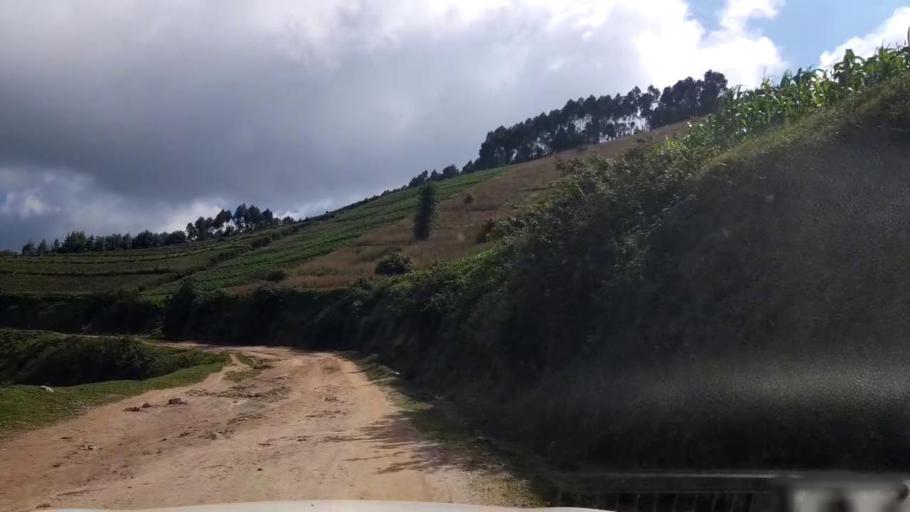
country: RW
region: Western Province
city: Kibuye
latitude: -1.8816
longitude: 29.4788
